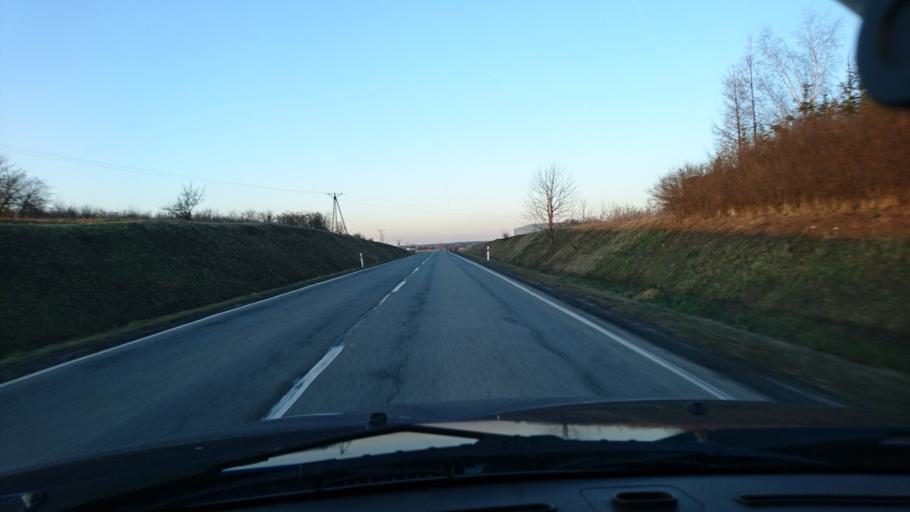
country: PL
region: Silesian Voivodeship
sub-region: Powiat gliwicki
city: Wielowies
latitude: 50.5072
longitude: 18.6046
